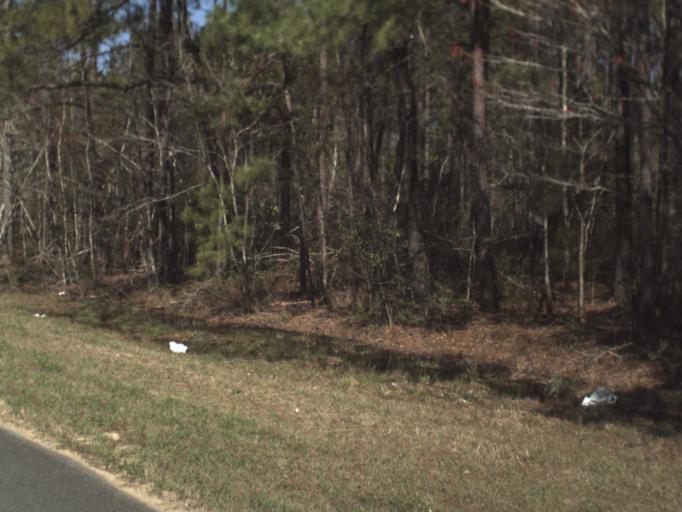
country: US
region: Florida
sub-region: Jackson County
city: Marianna
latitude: 30.7434
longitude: -85.1570
